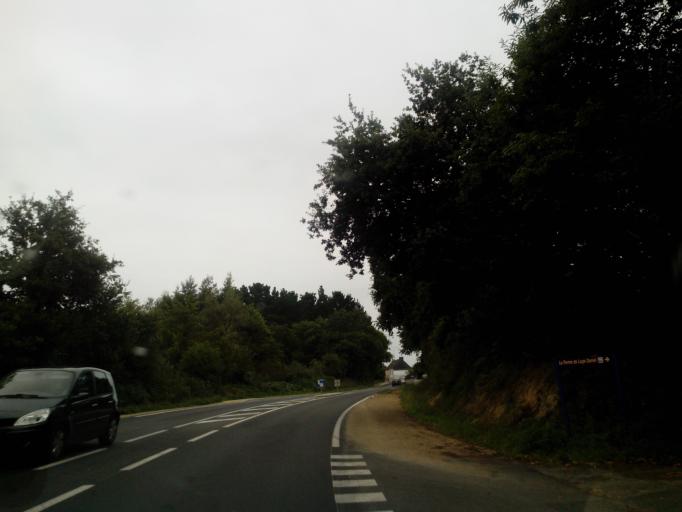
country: FR
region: Brittany
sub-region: Departement du Finistere
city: Quimperle
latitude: 47.8603
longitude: -3.5179
